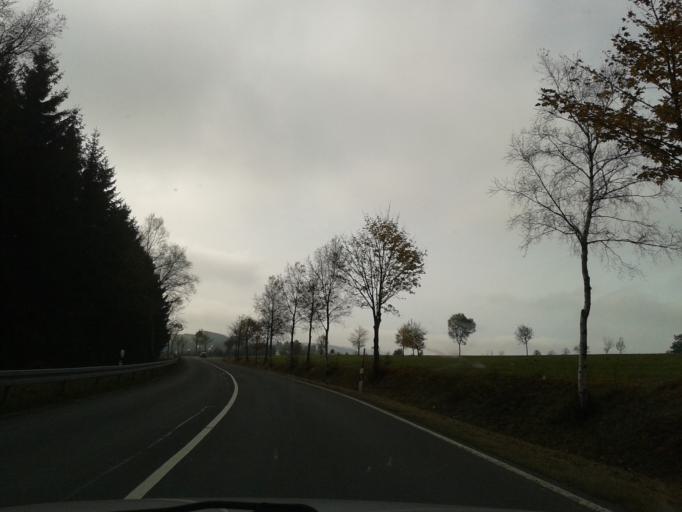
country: DE
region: North Rhine-Westphalia
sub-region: Regierungsbezirk Arnsberg
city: Winterberg
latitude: 51.1618
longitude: 8.4704
